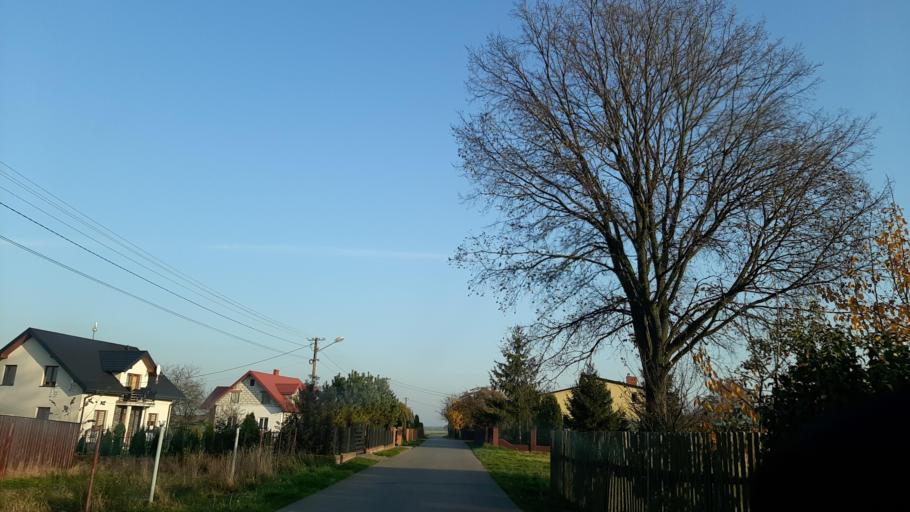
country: PL
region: Lublin Voivodeship
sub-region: Powiat lubelski
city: Garbow
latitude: 51.3840
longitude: 22.3410
